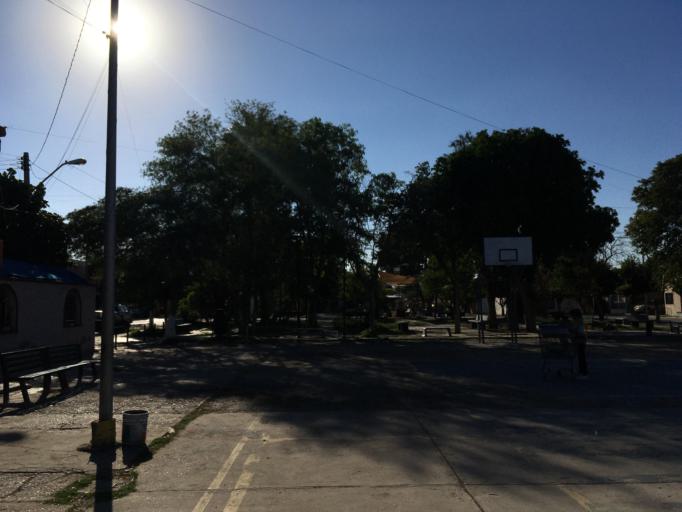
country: MX
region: Coahuila
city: Torreon
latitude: 25.5706
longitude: -103.4360
